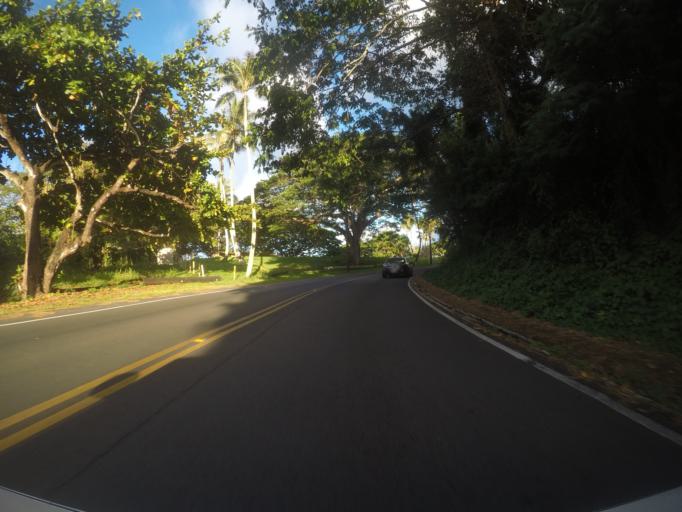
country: US
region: Hawaii
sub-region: Honolulu County
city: He'eia
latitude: 21.4415
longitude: -157.8103
